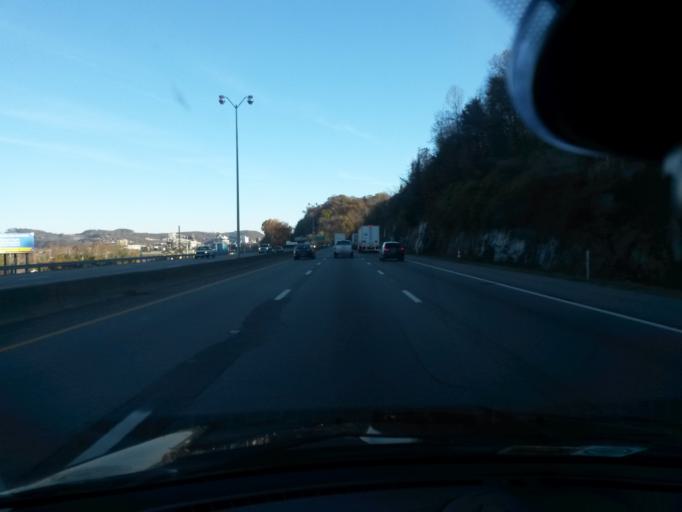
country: US
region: West Virginia
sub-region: Kanawha County
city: Charleston
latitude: 38.3604
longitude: -81.6653
